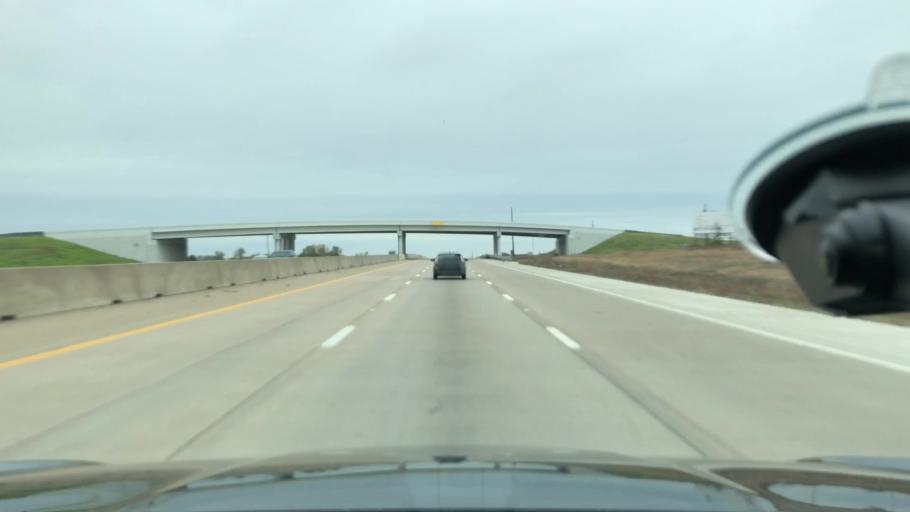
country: US
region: Texas
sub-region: Ellis County
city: Nash
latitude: 32.2980
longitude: -96.8650
